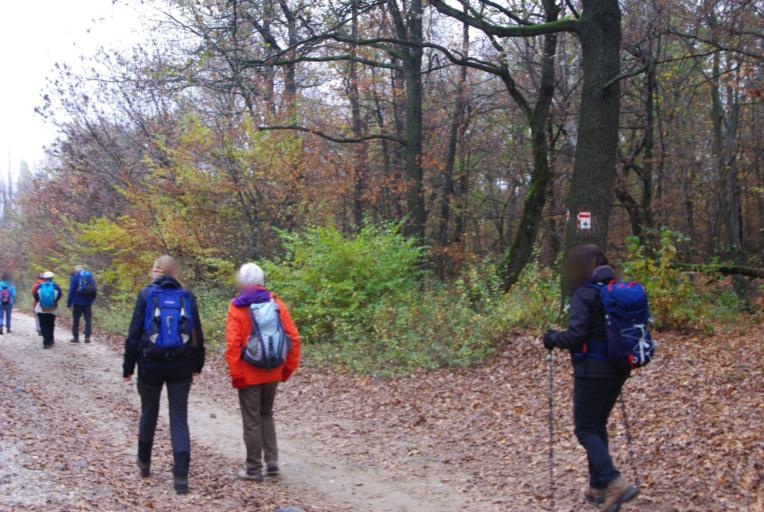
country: HU
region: Pest
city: Isaszeg
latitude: 47.5148
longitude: 19.4044
